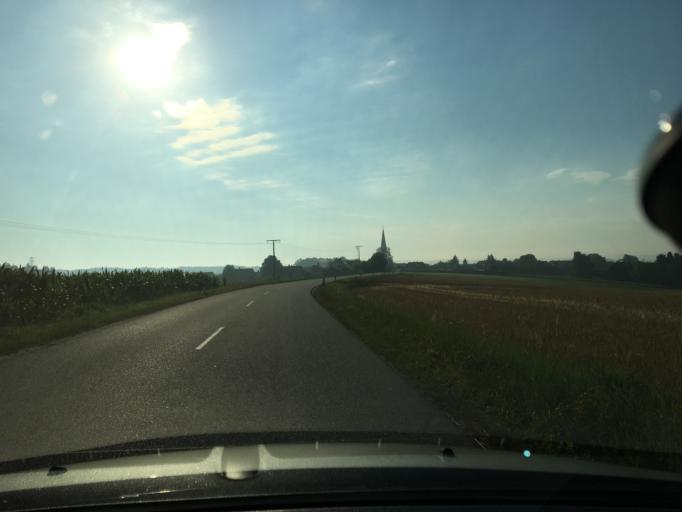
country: DE
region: Bavaria
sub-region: Lower Bavaria
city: Vilsbiburg
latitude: 48.4826
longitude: 12.3329
